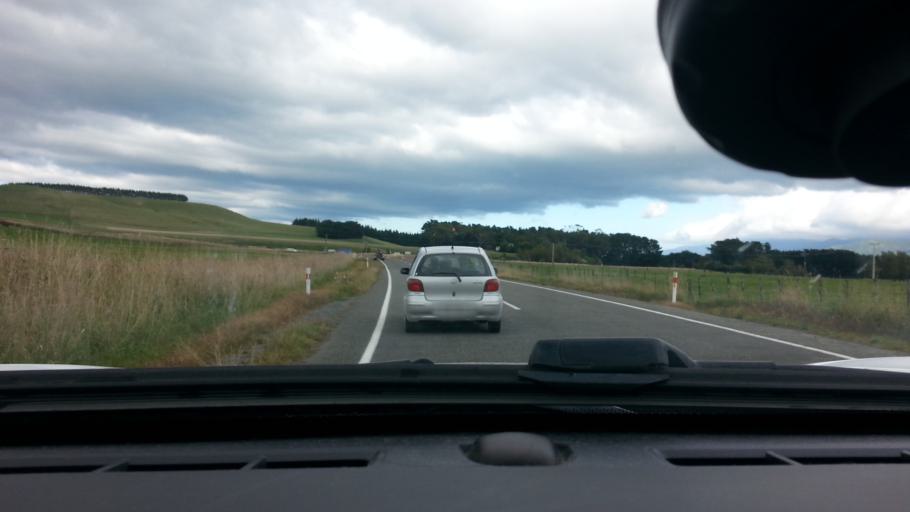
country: NZ
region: Wellington
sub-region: Upper Hutt City
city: Upper Hutt
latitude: -41.3701
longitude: 175.1777
